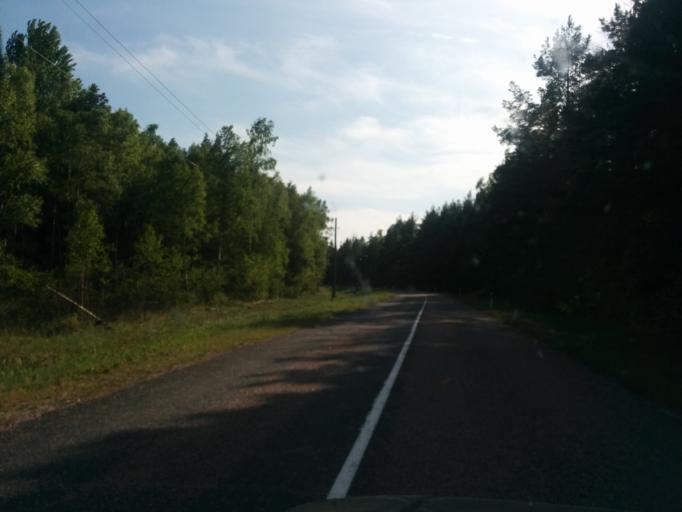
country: LV
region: Dundaga
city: Dundaga
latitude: 57.6540
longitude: 22.2710
